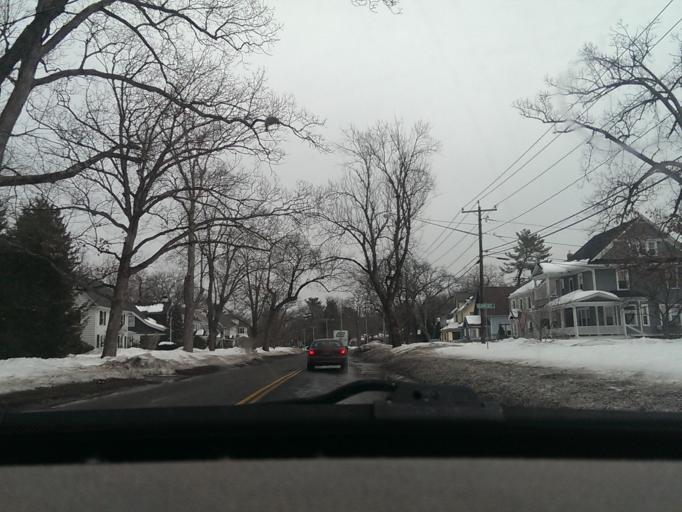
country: US
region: Massachusetts
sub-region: Hampden County
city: Longmeadow
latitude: 42.0650
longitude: -72.5760
